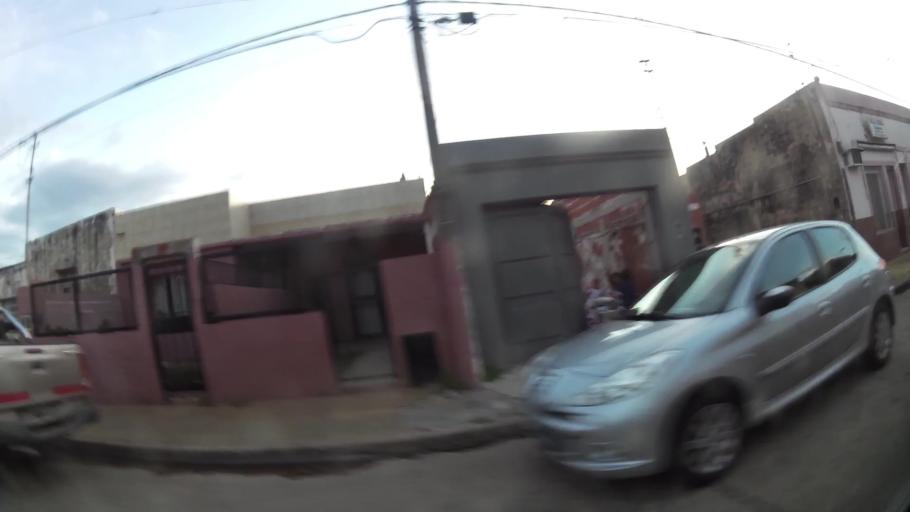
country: AR
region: Buenos Aires
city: San Nicolas de los Arroyos
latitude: -33.3296
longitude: -60.2248
